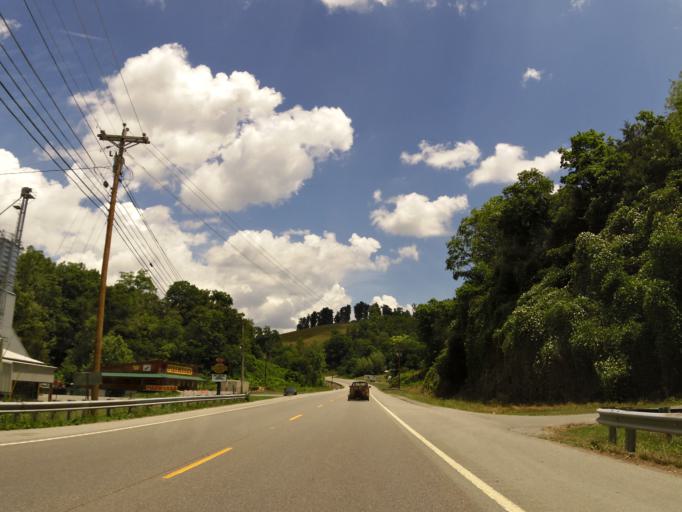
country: US
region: Tennessee
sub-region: Claiborne County
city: New Tazewell
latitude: 36.3916
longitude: -83.7029
